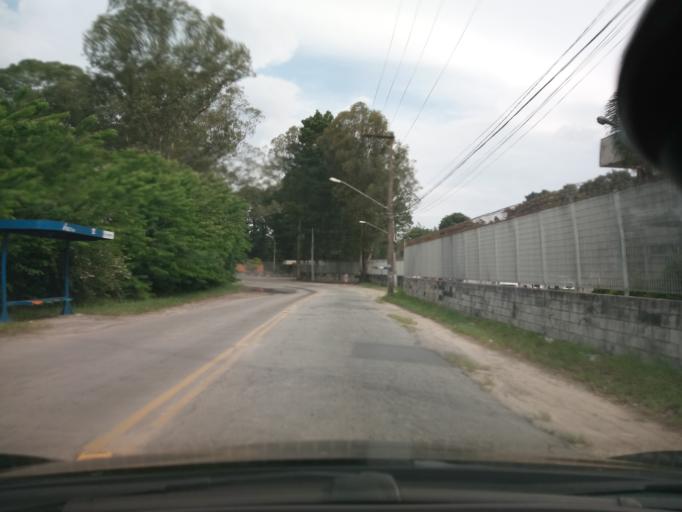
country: BR
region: Sao Paulo
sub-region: Sao Bernardo Do Campo
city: Sao Bernardo do Campo
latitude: -23.7477
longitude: -46.5950
